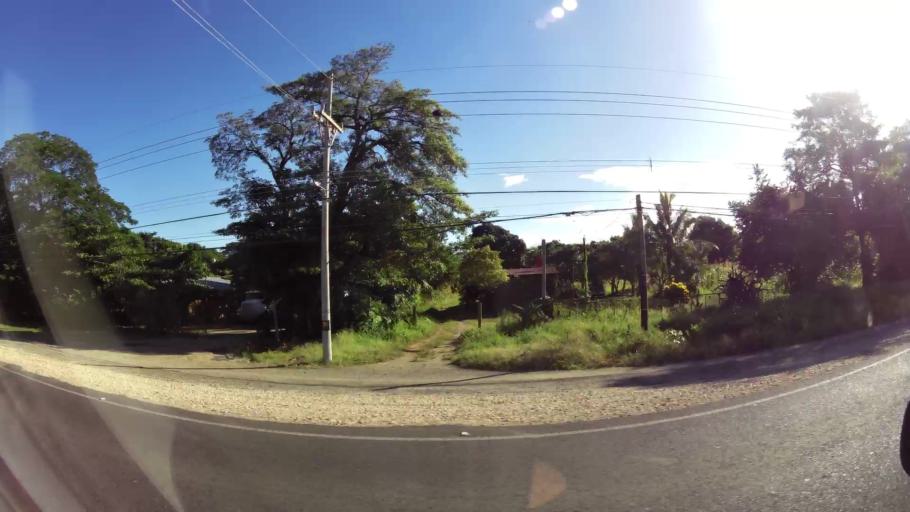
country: CR
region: Guanacaste
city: Belen
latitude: 10.4665
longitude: -85.5607
